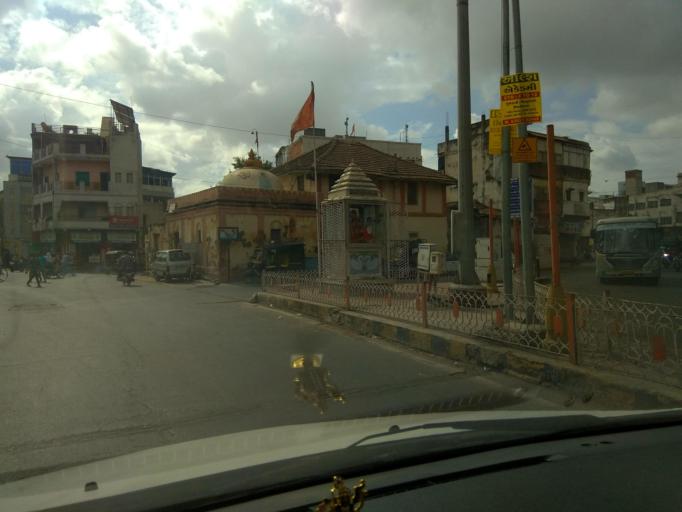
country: IN
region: Gujarat
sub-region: Bhavnagar
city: Bhavnagar
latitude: 21.7738
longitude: 72.1461
